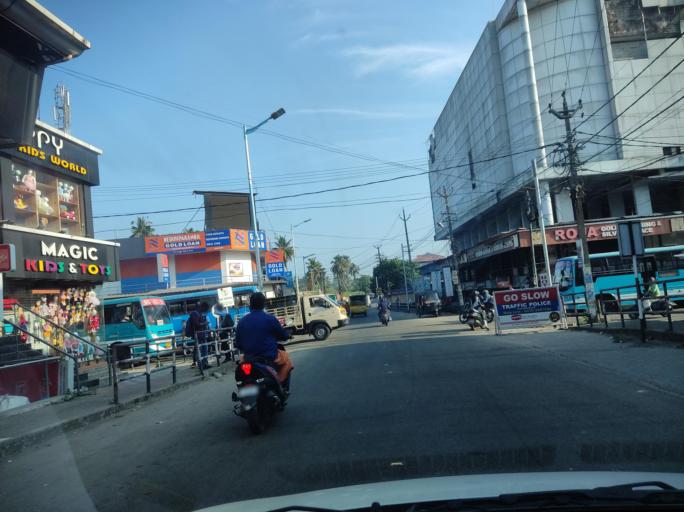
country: IN
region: Kerala
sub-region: Alappuzha
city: Kayankulam
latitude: 9.1735
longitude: 76.5000
